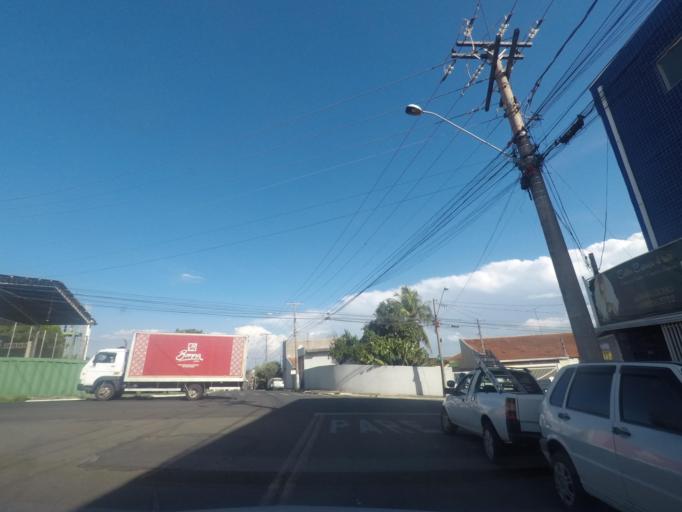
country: BR
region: Sao Paulo
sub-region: Sumare
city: Sumare
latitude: -22.8117
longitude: -47.2658
